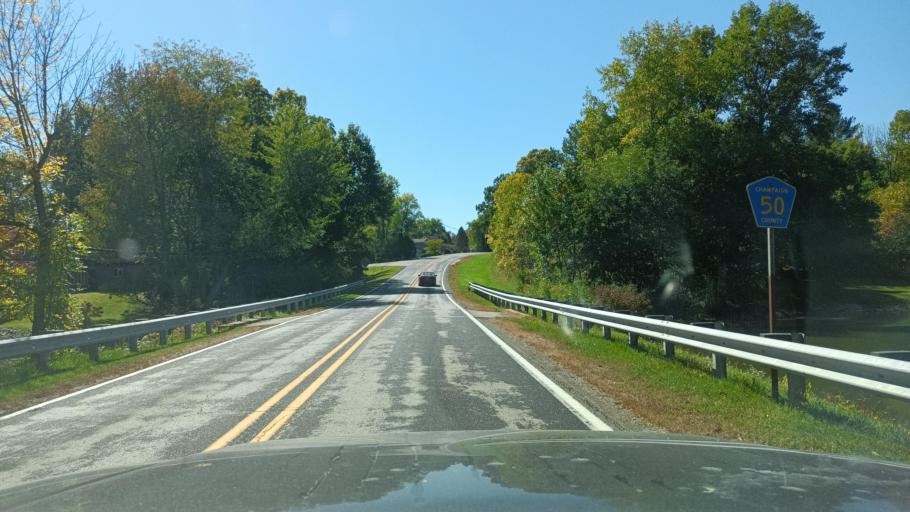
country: US
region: Illinois
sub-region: Champaign County
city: Lake of the Woods
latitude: 40.1975
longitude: -88.3784
